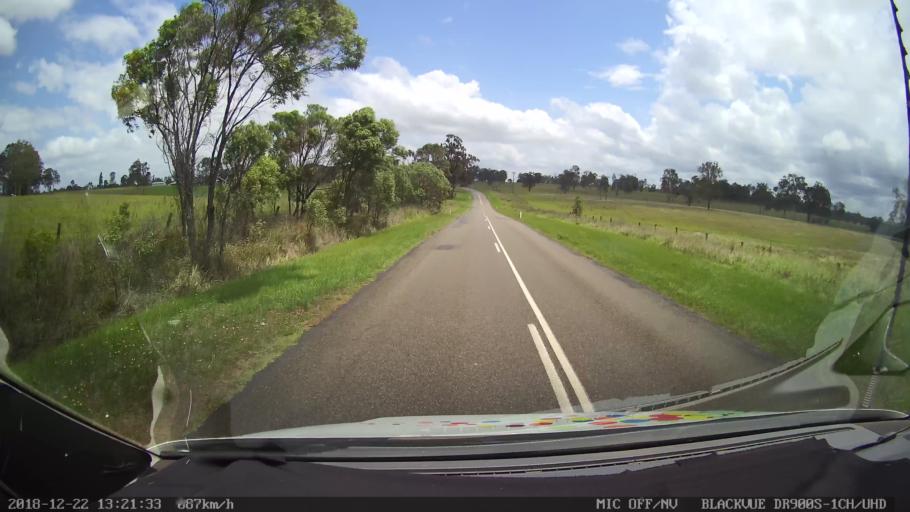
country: AU
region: New South Wales
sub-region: Clarence Valley
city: Coutts Crossing
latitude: -29.7781
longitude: 152.9192
